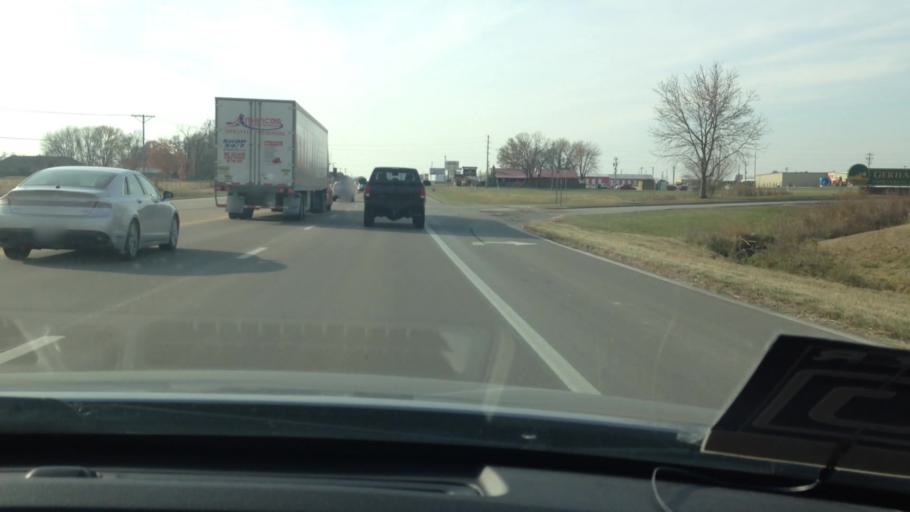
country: US
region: Missouri
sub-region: Henry County
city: Clinton
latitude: 38.3891
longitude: -93.7899
